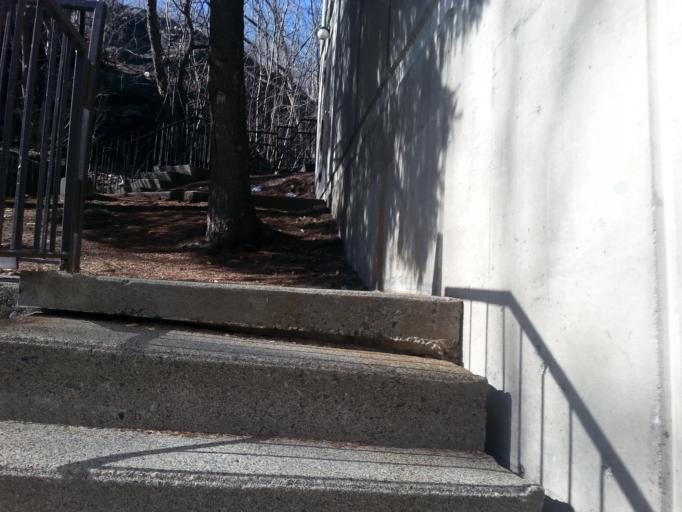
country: CA
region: Ontario
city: Greater Sudbury
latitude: 46.4959
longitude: -80.9930
